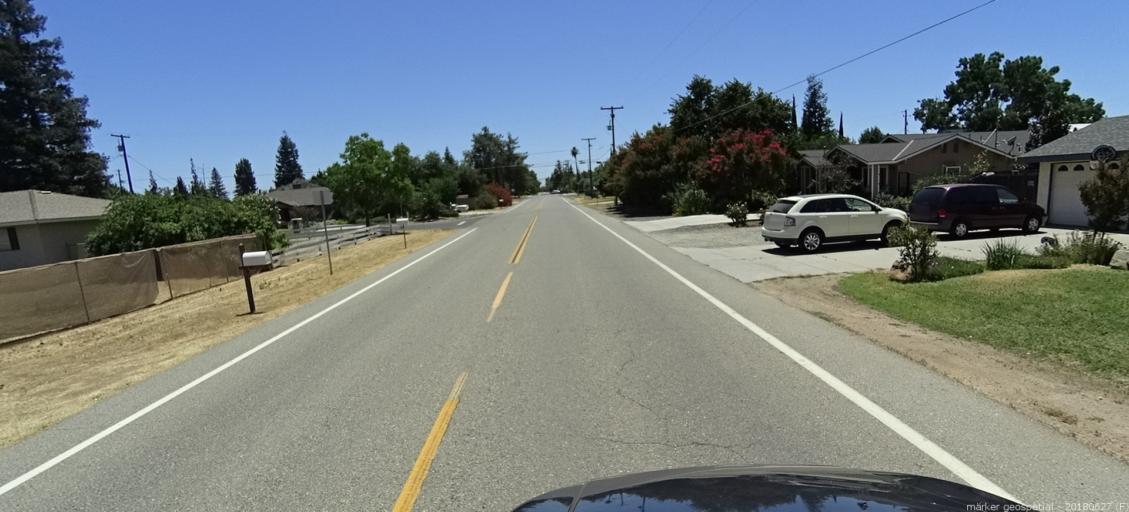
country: US
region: California
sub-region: Madera County
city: Bonadelle Ranchos-Madera Ranchos
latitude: 36.9253
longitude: -119.8852
